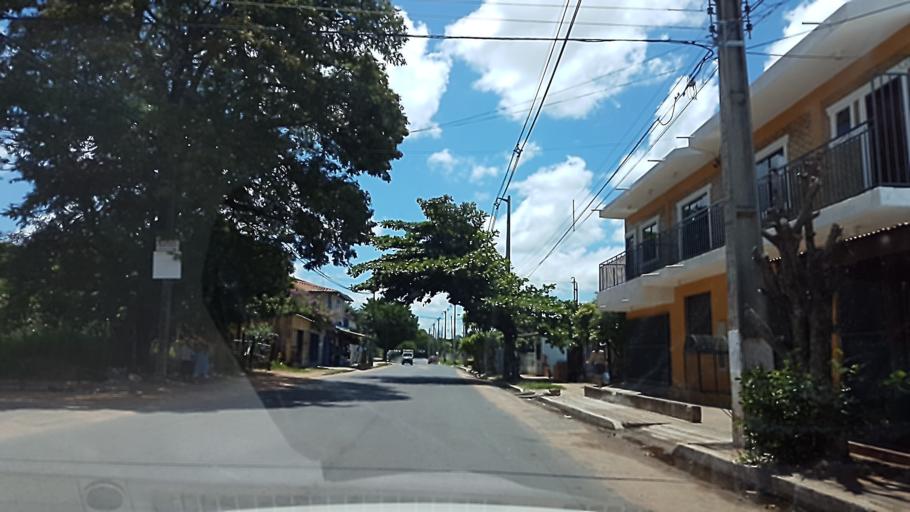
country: PY
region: Central
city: Colonia Mariano Roque Alonso
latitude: -25.2450
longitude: -57.5316
